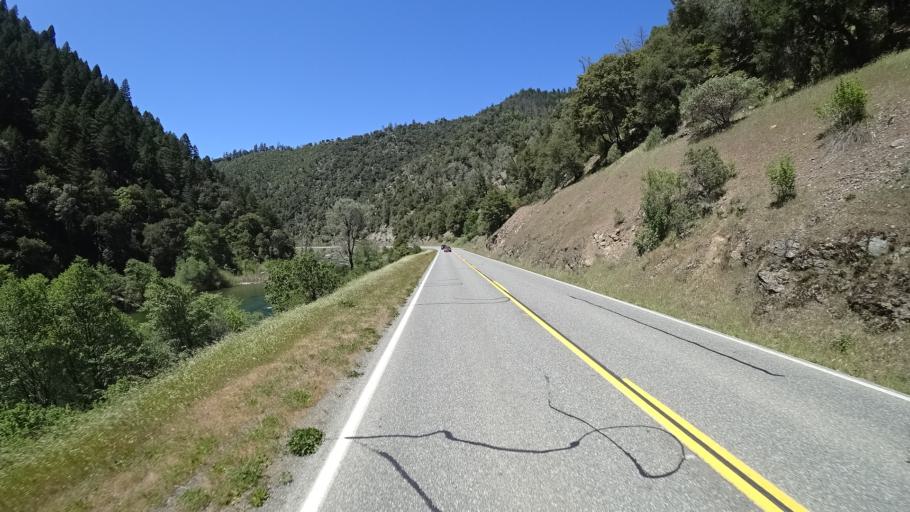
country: US
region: California
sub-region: Trinity County
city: Hayfork
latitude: 40.7649
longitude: -123.2913
